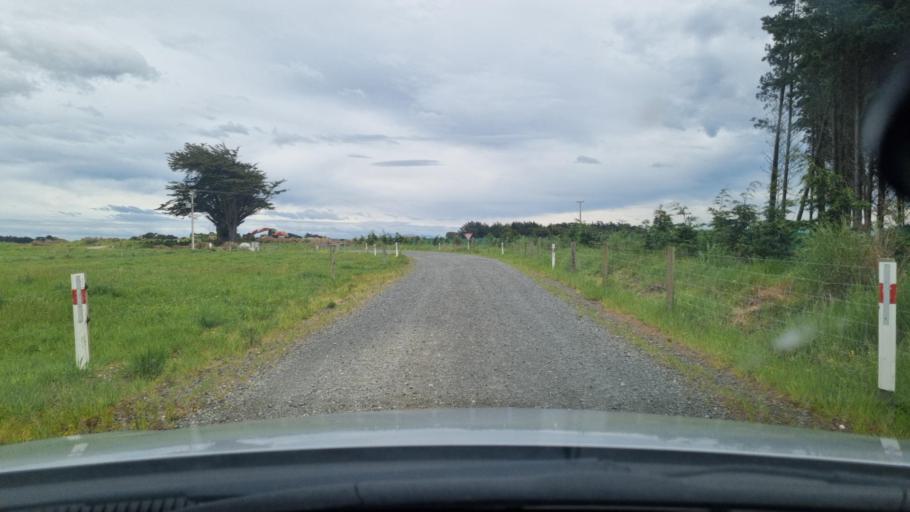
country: NZ
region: Southland
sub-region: Invercargill City
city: Invercargill
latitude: -46.4082
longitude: 168.2736
